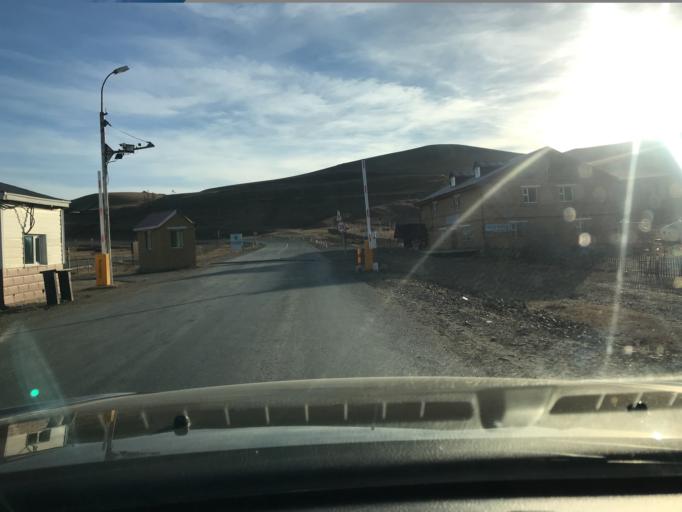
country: MN
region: Central Aimak
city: Dzuunmod
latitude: 47.8168
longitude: 107.3294
